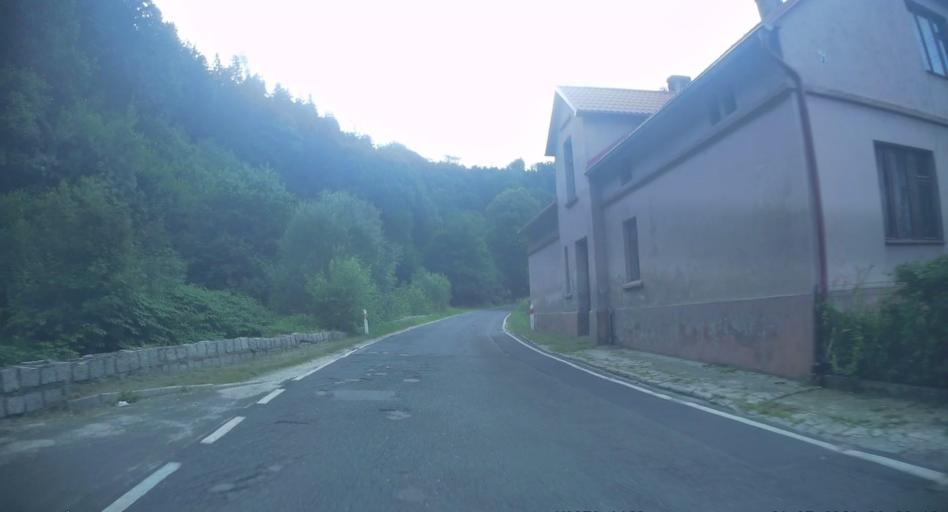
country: PL
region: Lower Silesian Voivodeship
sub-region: Powiat walbrzyski
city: Walim
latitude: 50.7151
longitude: 16.4316
